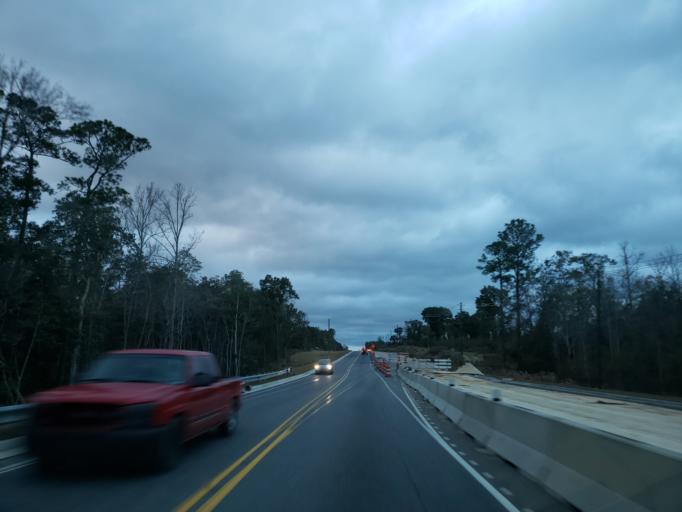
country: US
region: Alabama
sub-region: Mobile County
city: Chickasaw
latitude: 30.7811
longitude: -88.2258
